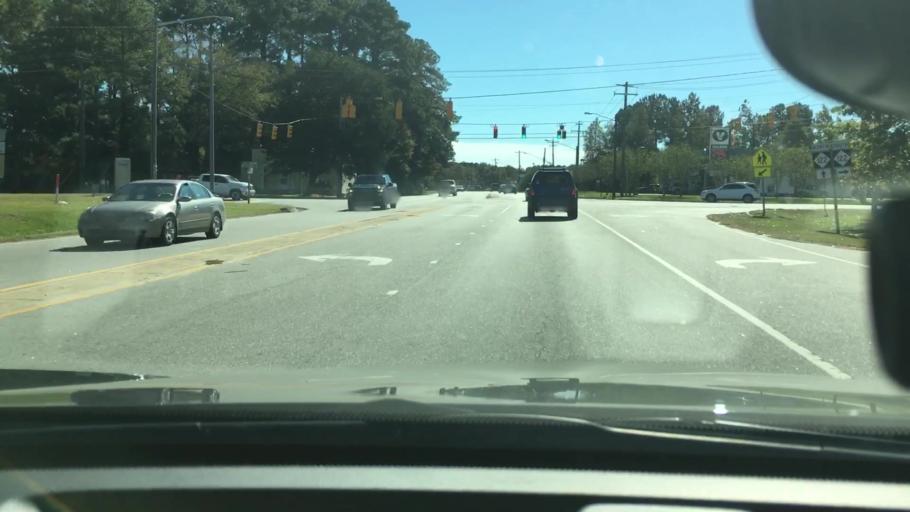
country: US
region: North Carolina
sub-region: Edgecombe County
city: Tarboro
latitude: 35.9002
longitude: -77.5604
